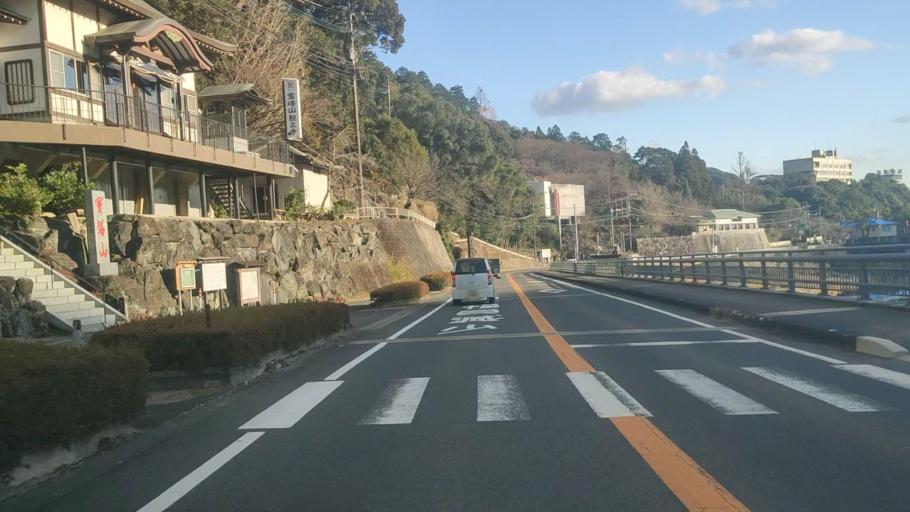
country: JP
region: Saga Prefecture
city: Saga-shi
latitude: 33.3311
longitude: 130.2670
